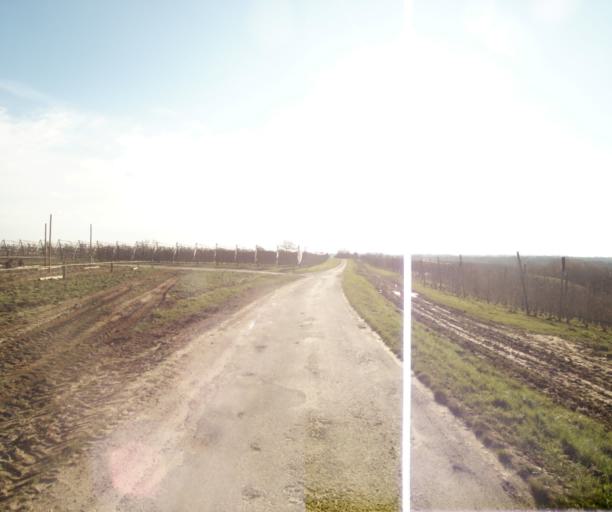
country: FR
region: Midi-Pyrenees
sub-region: Departement du Tarn-et-Garonne
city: Moissac
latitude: 44.1352
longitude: 1.0550
